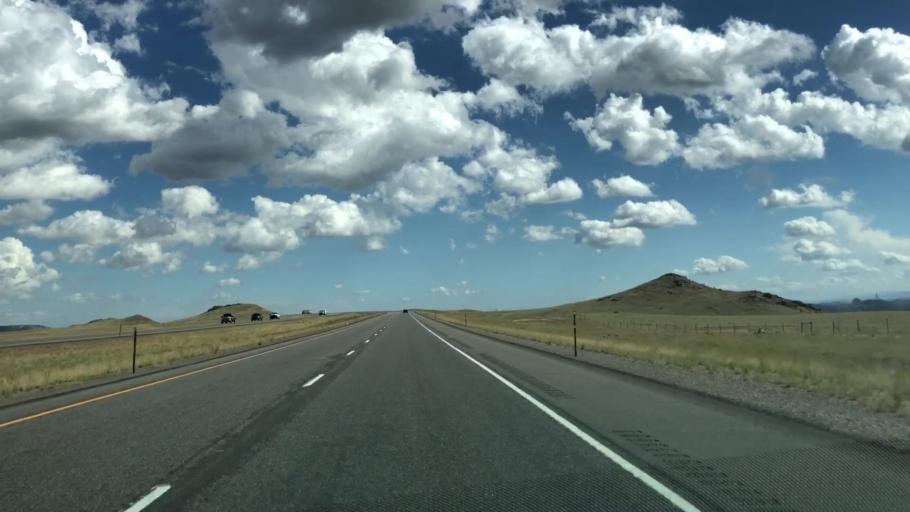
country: US
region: Wyoming
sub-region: Albany County
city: Laramie
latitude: 41.0480
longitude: -105.4651
